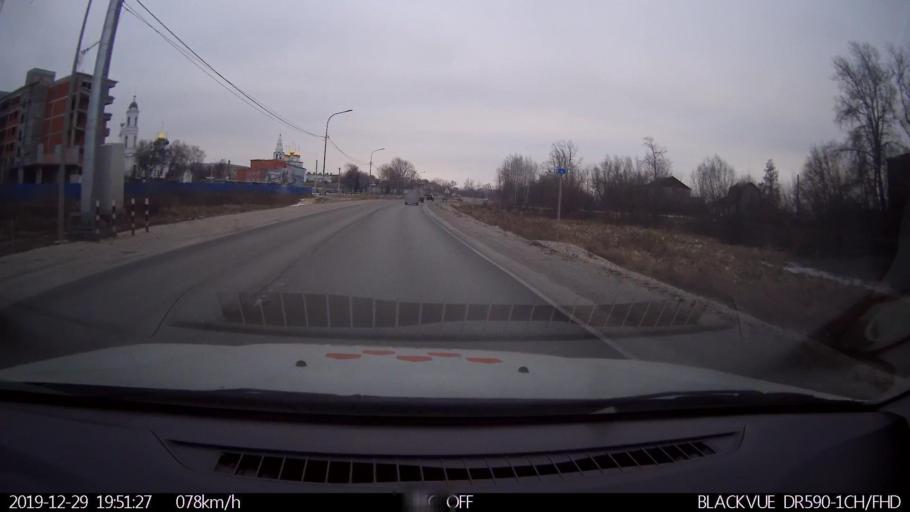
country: RU
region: Nizjnij Novgorod
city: Bor
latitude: 56.3598
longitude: 44.0427
